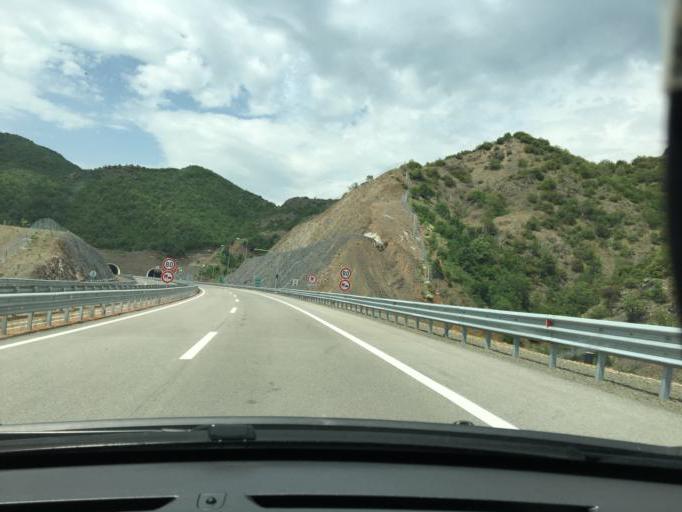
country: MK
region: Demir Kapija
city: Demir Kapija
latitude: 41.3732
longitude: 22.3269
